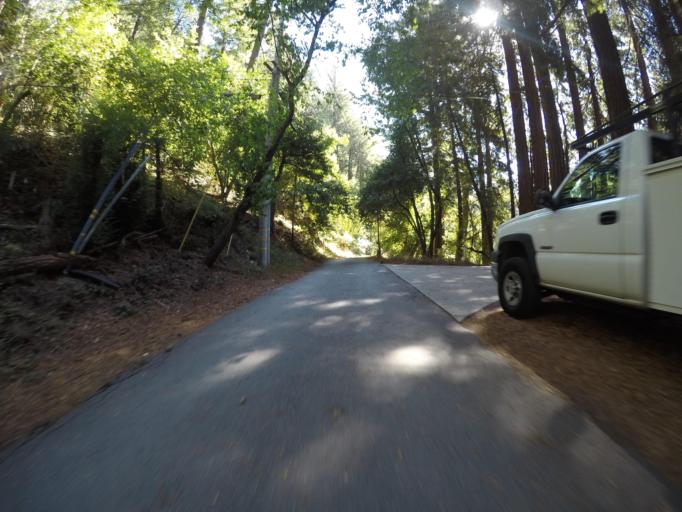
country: US
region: California
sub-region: Santa Cruz County
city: Scotts Valley
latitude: 37.0574
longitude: -122.0196
